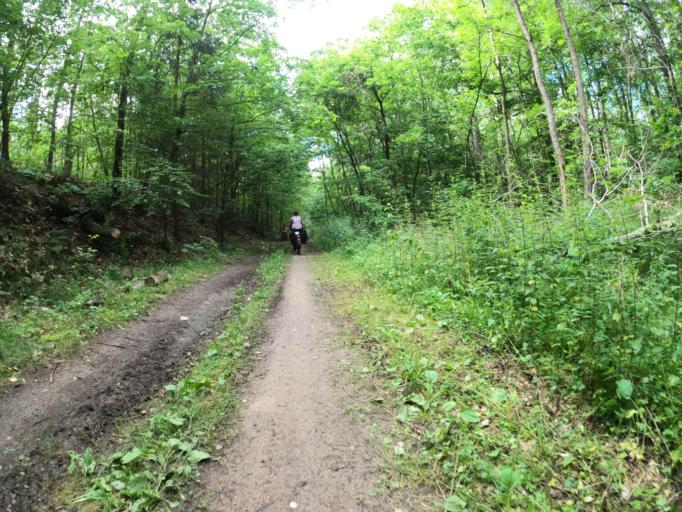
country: PL
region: West Pomeranian Voivodeship
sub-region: Powiat bialogardzki
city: Tychowo
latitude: 54.0046
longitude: 16.3659
